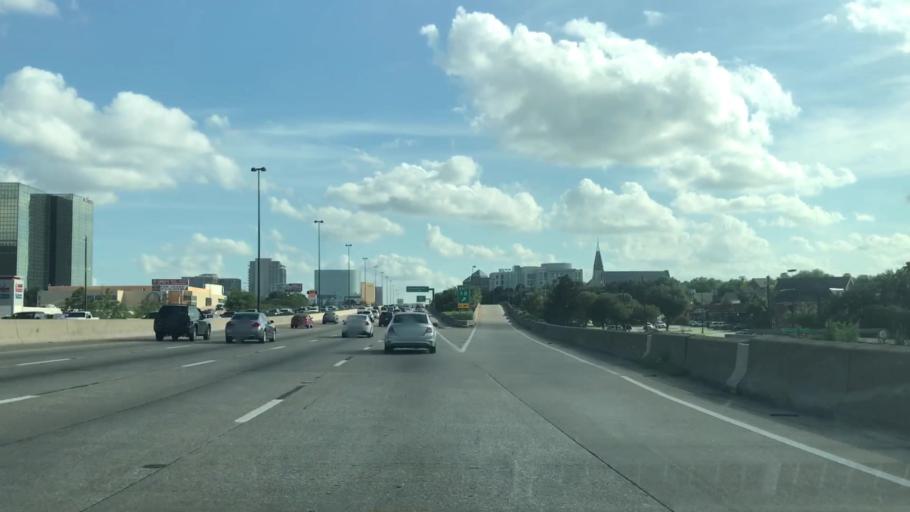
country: US
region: Texas
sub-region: Dallas County
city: University Park
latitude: 32.8806
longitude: -96.7703
